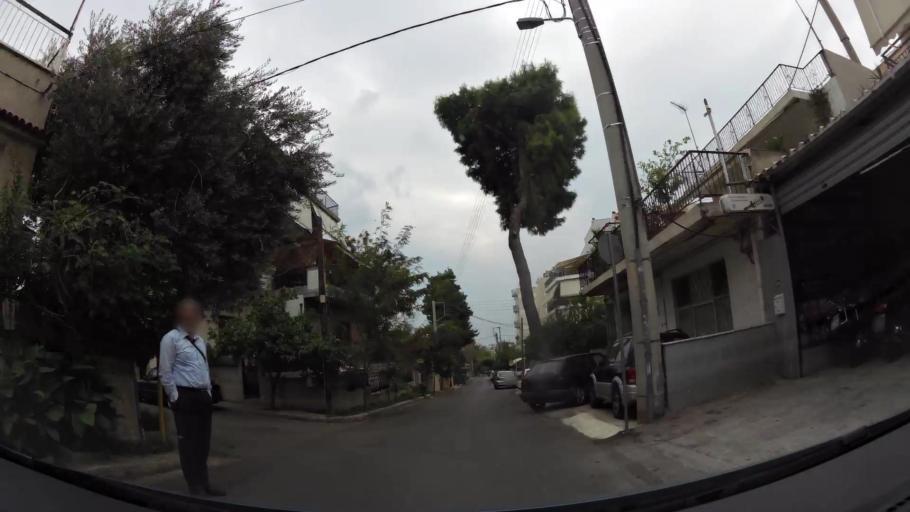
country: GR
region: Attica
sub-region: Nomarchia Athinas
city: Agios Dimitrios
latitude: 37.9291
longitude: 23.7198
